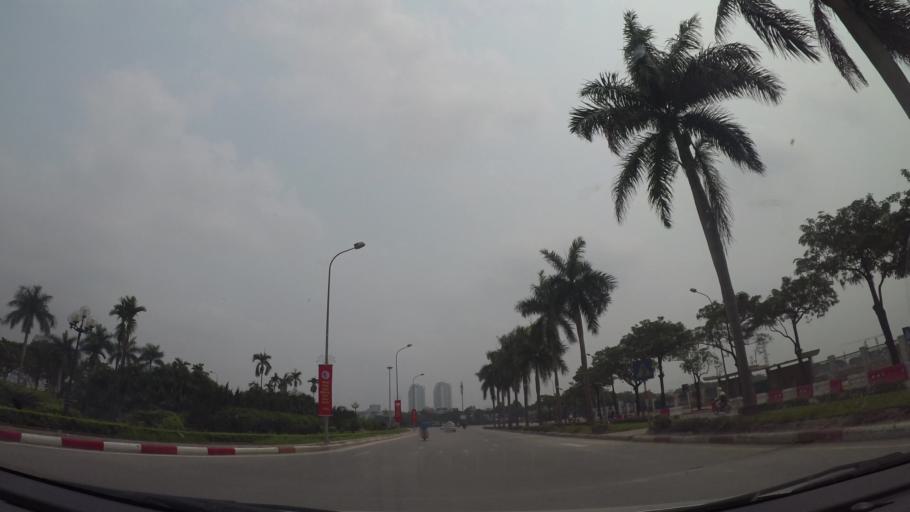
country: VN
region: Ha Noi
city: Cau Dien
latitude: 21.0187
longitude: 105.7665
